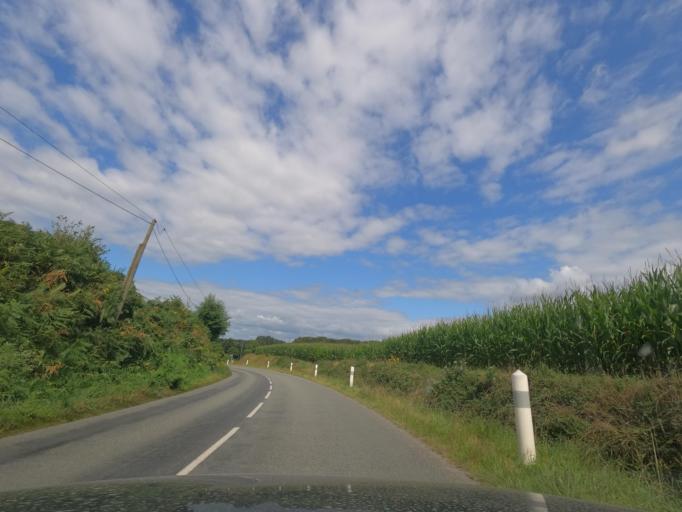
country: FR
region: Pays de la Loire
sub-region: Departement de la Mayenne
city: Landivy
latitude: 48.4494
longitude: -1.0676
